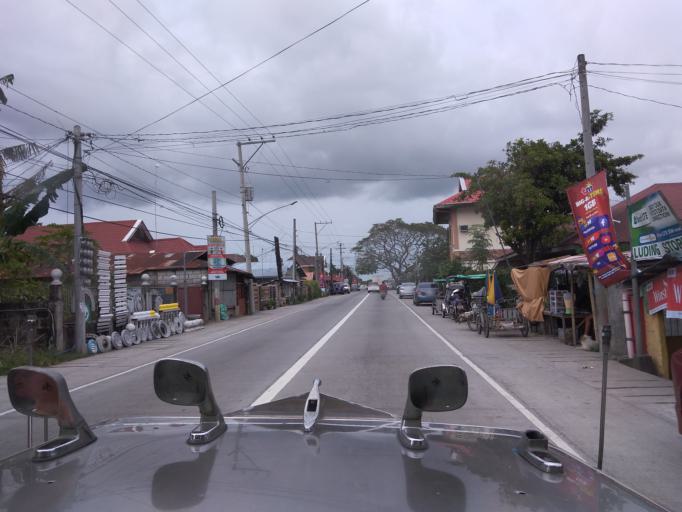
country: PH
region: Central Luzon
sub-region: Province of Pampanga
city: Pandacaqui
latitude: 15.1887
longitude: 120.6348
